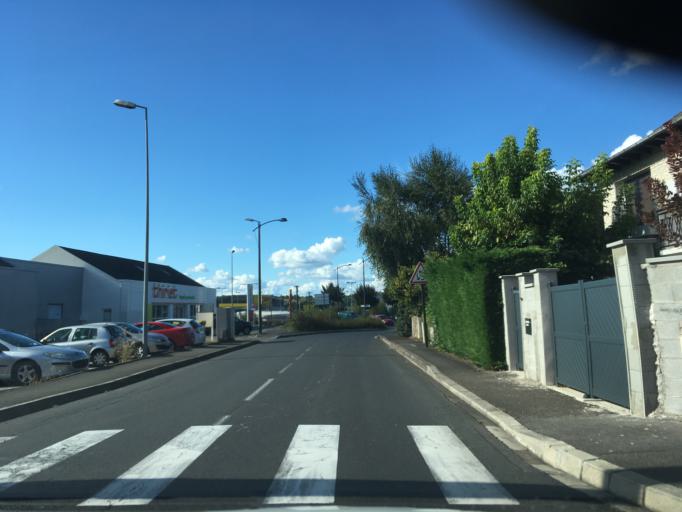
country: FR
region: Limousin
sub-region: Departement de la Correze
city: Brive-la-Gaillarde
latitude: 45.1517
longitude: 1.5055
